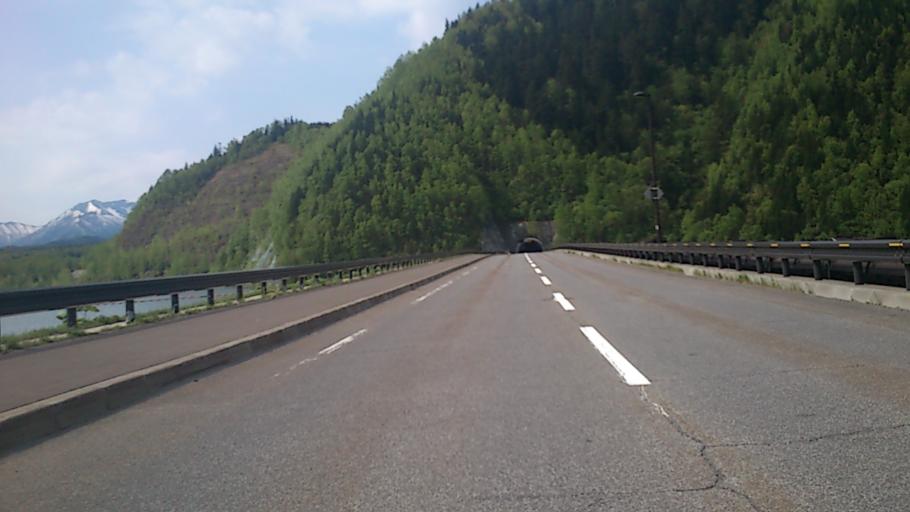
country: JP
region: Hokkaido
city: Kamikawa
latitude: 43.6777
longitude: 143.0375
